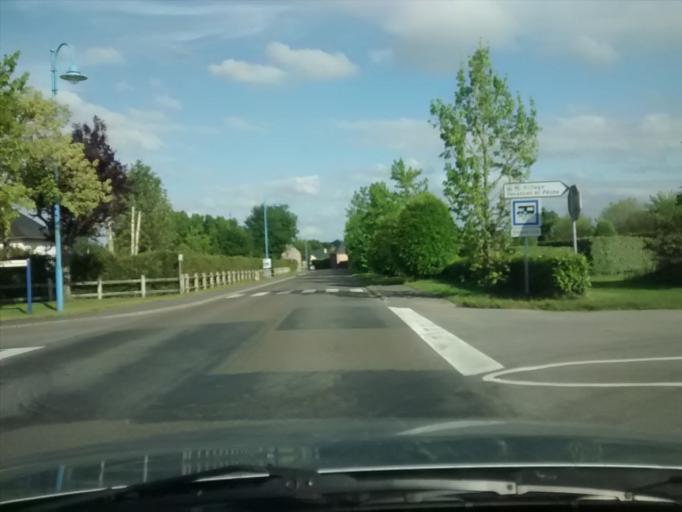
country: FR
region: Pays de la Loire
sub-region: Departement de la Mayenne
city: Entrammes
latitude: 47.9233
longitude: -0.6846
